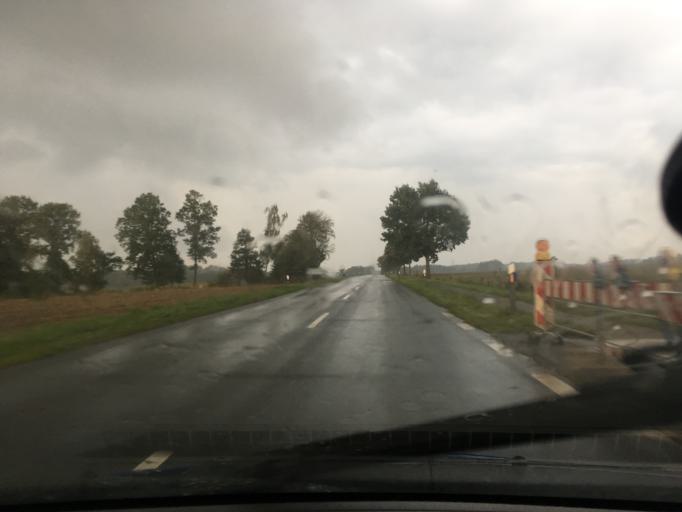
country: DE
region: Lower Saxony
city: Soderstorf
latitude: 53.1547
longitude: 10.1552
